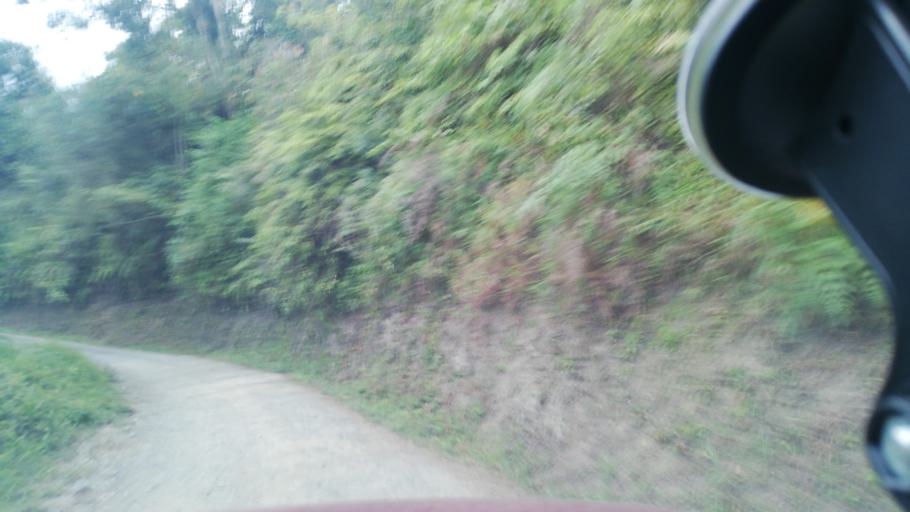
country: CO
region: Cundinamarca
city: Vergara
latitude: 5.1683
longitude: -74.2631
